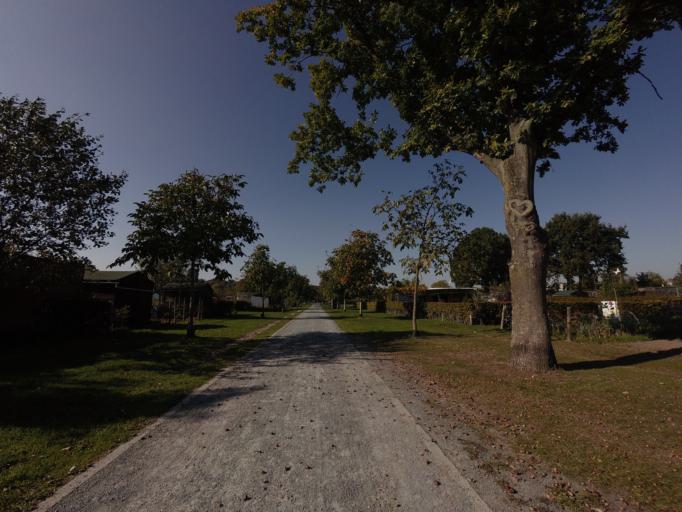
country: BE
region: Flanders
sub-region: Provincie Antwerpen
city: Borsbeek
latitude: 51.1964
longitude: 4.4712
